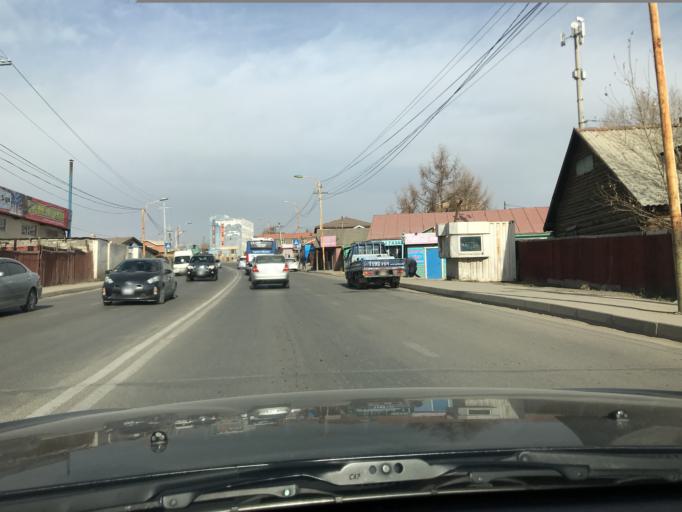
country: MN
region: Ulaanbaatar
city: Ulaanbaatar
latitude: 47.9324
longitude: 106.8874
